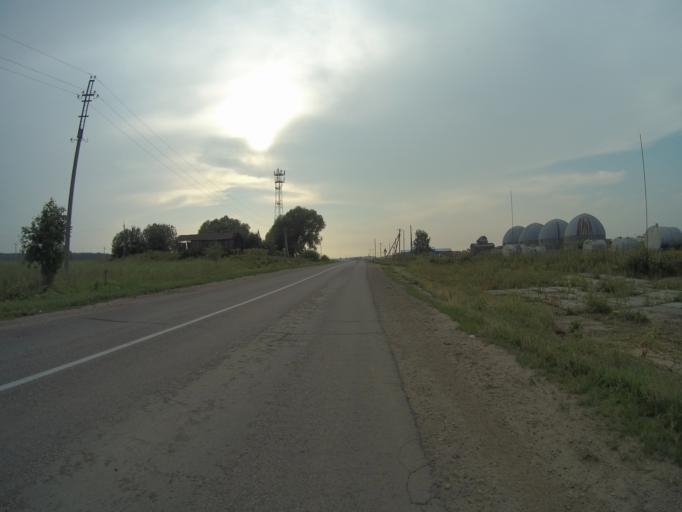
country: RU
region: Ivanovo
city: Gavrilov Posad
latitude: 56.3451
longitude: 40.1867
